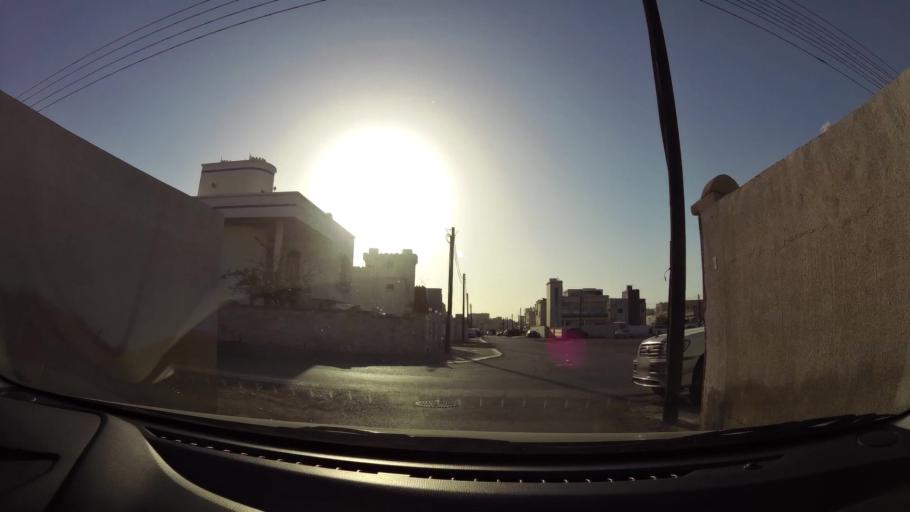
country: OM
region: Muhafazat Masqat
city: As Sib al Jadidah
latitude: 23.6284
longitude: 58.1953
